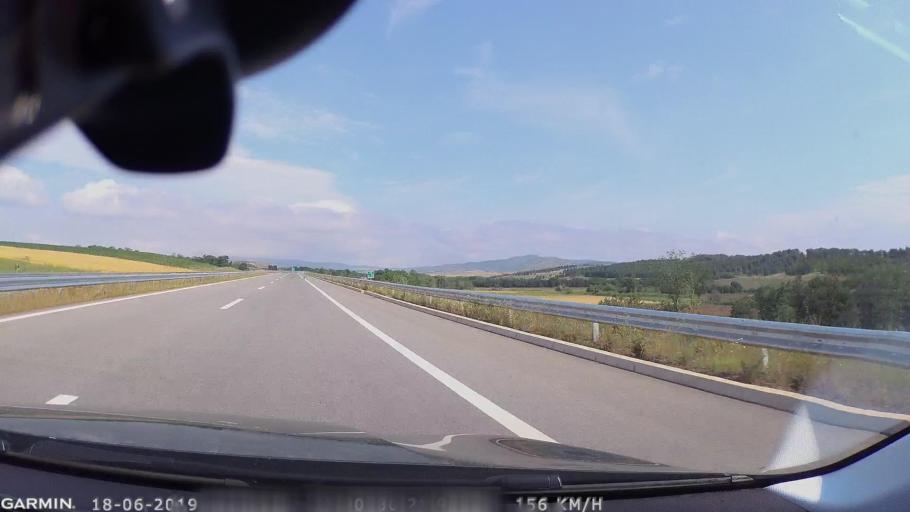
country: MK
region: Sveti Nikole
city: Gorobinci
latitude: 41.9064
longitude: 21.9074
